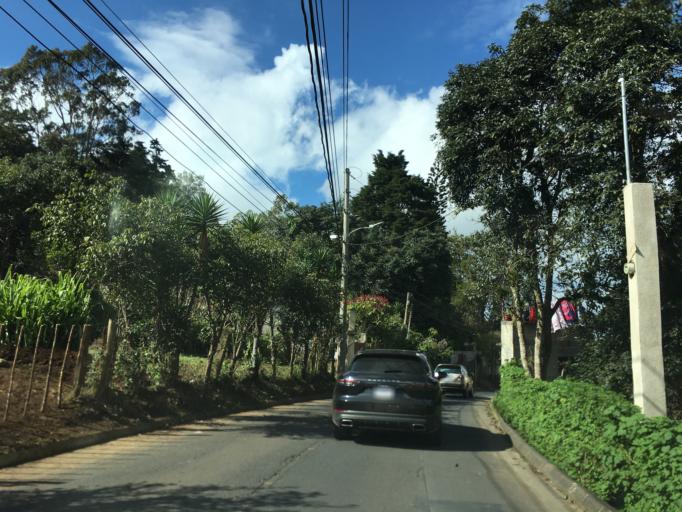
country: GT
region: Guatemala
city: San Jose Pinula
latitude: 14.5680
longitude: -90.4398
